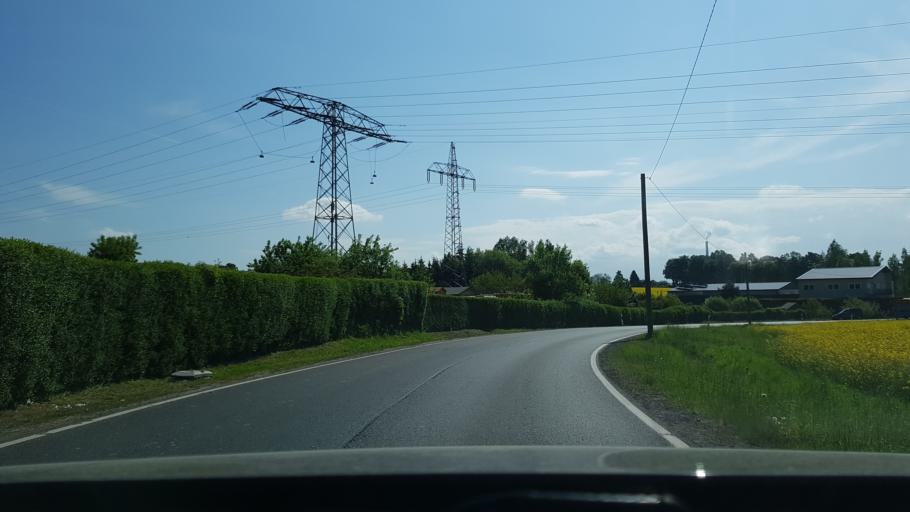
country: DE
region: Saxony
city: Wittgensdorf
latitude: 50.8733
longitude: 12.8727
